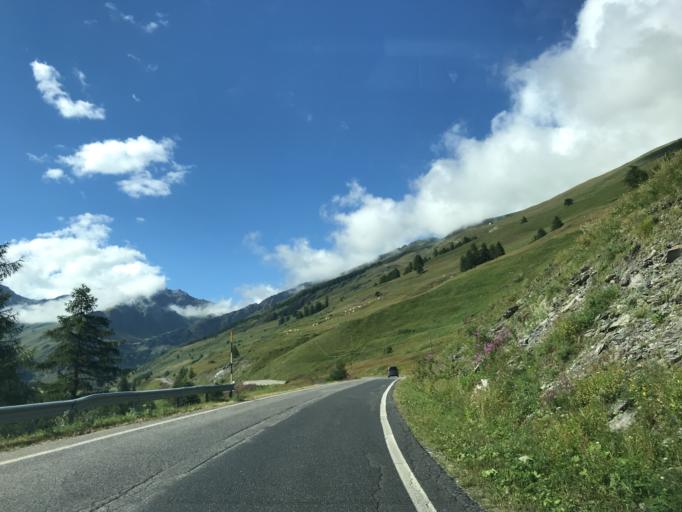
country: IT
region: Piedmont
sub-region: Provincia di Cuneo
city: Pontechianale
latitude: 44.6317
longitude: 7.0173
